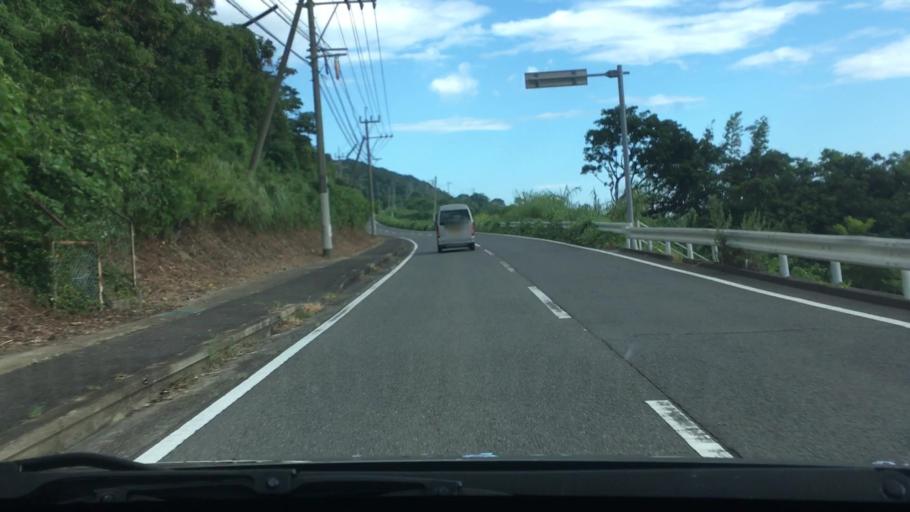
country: JP
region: Nagasaki
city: Togitsu
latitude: 32.8676
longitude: 129.6810
